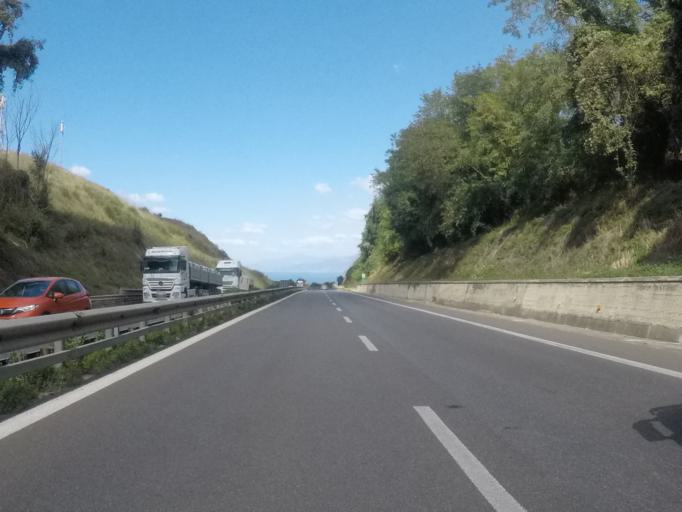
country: IT
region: Calabria
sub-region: Provincia di Vibo-Valentia
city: Sant'Onofrio
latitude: 38.7098
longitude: 16.1539
